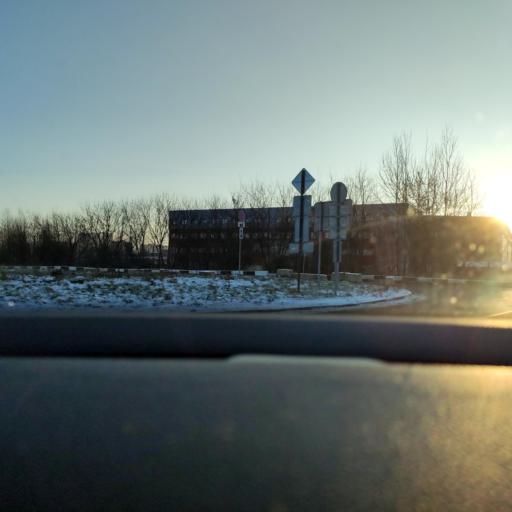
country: RU
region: Moskovskaya
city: Kotel'niki
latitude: 55.6516
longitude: 37.8394
